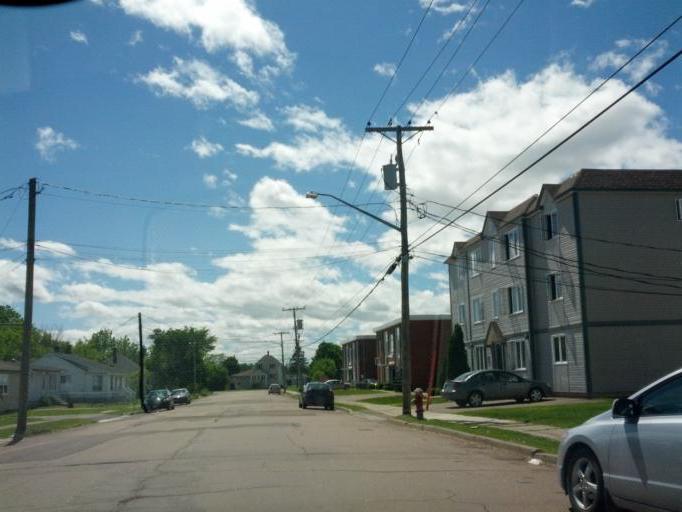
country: CA
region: New Brunswick
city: Moncton
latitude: 46.1130
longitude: -64.7787
